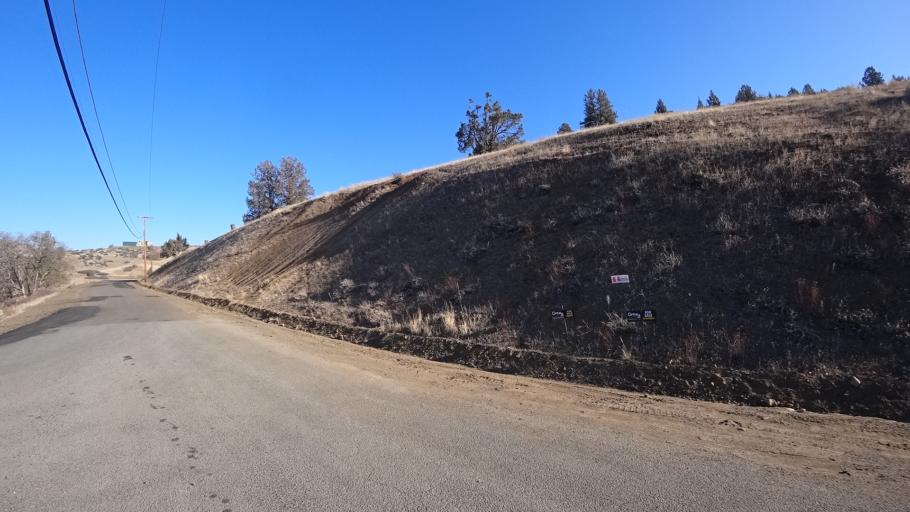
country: US
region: California
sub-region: Siskiyou County
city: Montague
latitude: 41.8906
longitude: -122.4809
